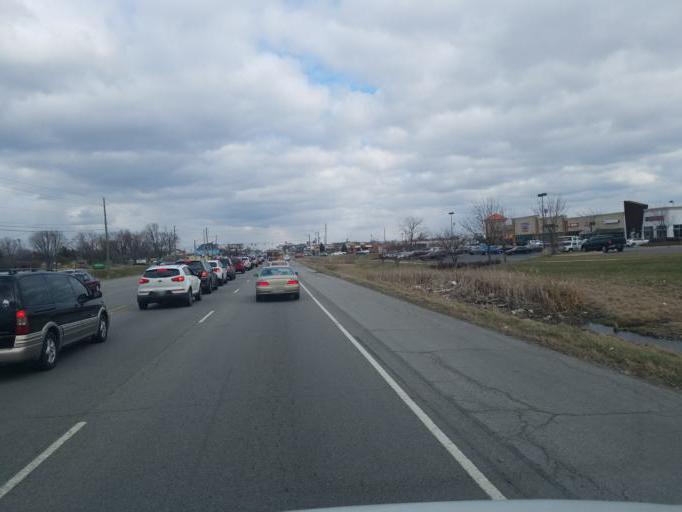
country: US
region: Indiana
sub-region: Marion County
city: Clermont
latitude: 39.7636
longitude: -86.3394
